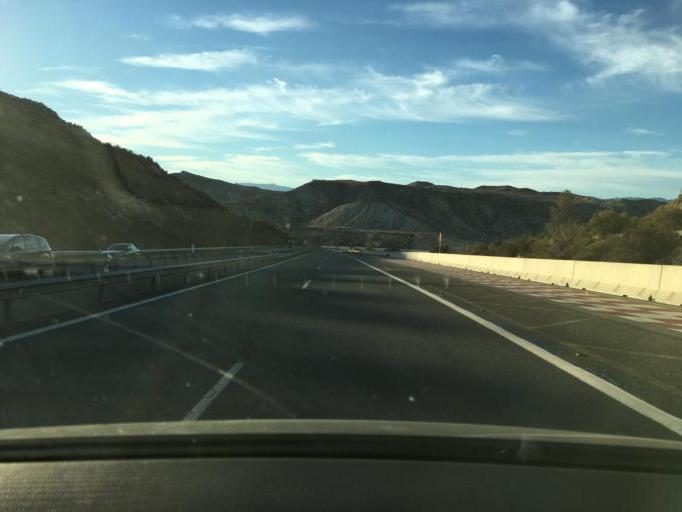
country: ES
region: Andalusia
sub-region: Provincia de Almeria
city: Sorbas
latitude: 37.0847
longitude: -2.0587
